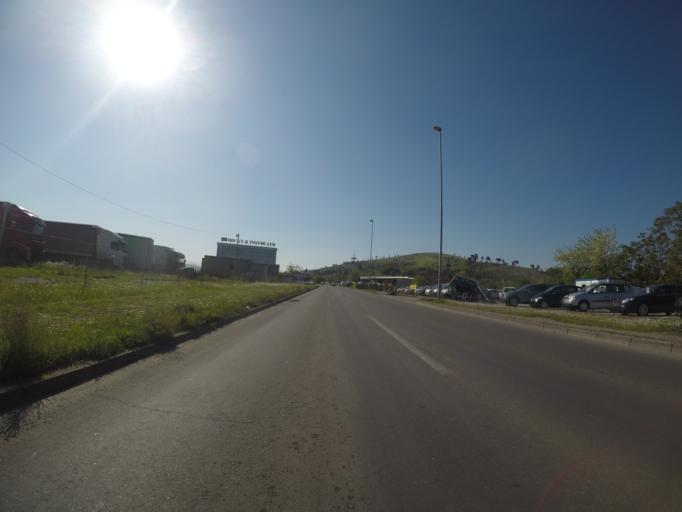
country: ME
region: Podgorica
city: Podgorica
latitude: 42.4276
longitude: 19.2332
